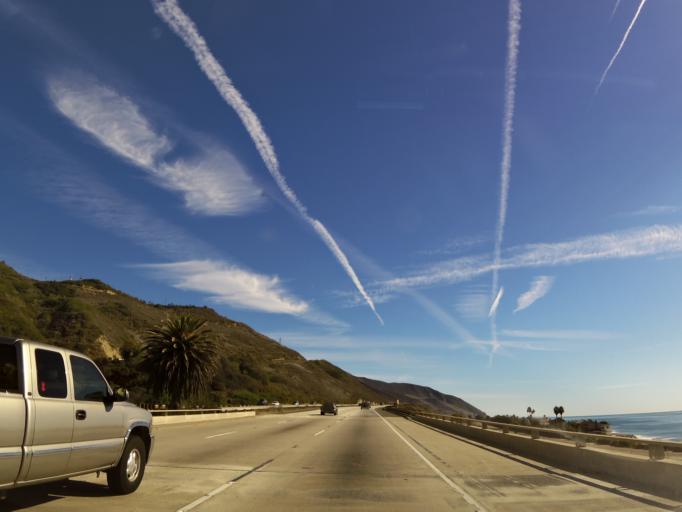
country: US
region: California
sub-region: Ventura County
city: Ventura
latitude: 34.3183
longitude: -119.3659
